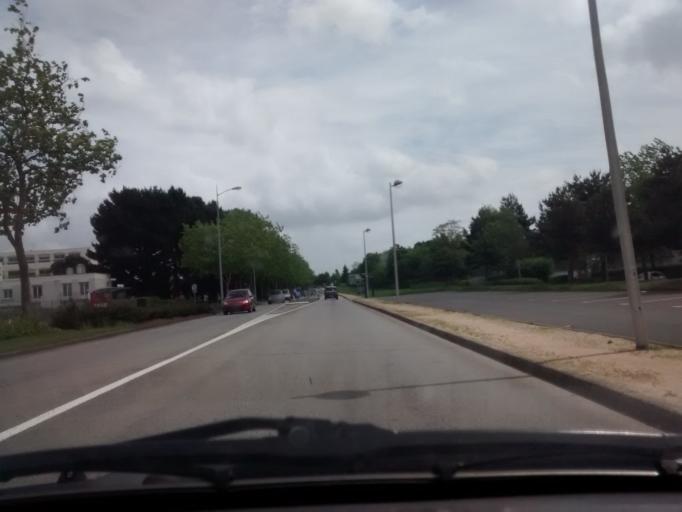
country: FR
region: Brittany
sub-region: Departement du Morbihan
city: Vannes
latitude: 47.6450
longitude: -2.7790
